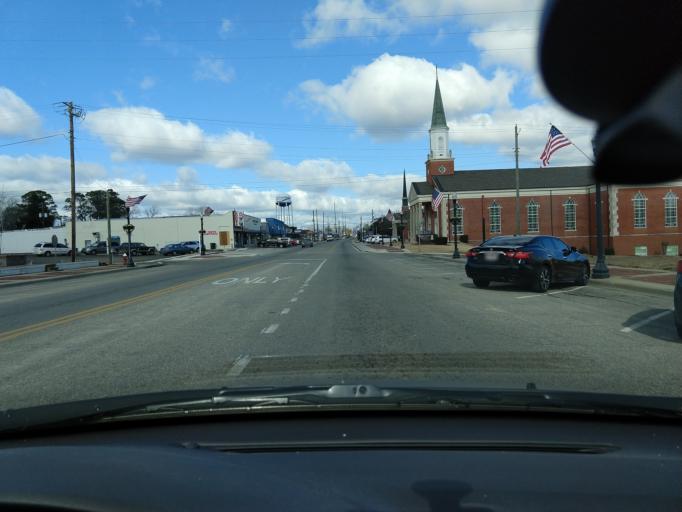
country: US
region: Alabama
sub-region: Coffee County
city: Enterprise
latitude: 31.3160
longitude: -85.8554
